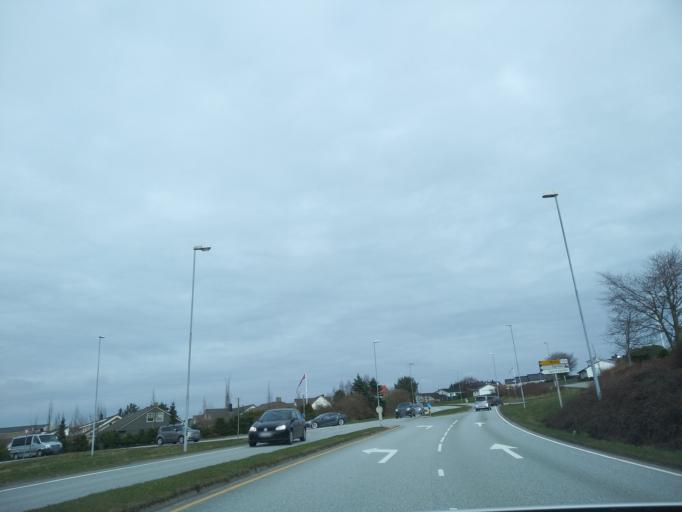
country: NO
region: Rogaland
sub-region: Sola
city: Sola
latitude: 58.9118
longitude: 5.6776
